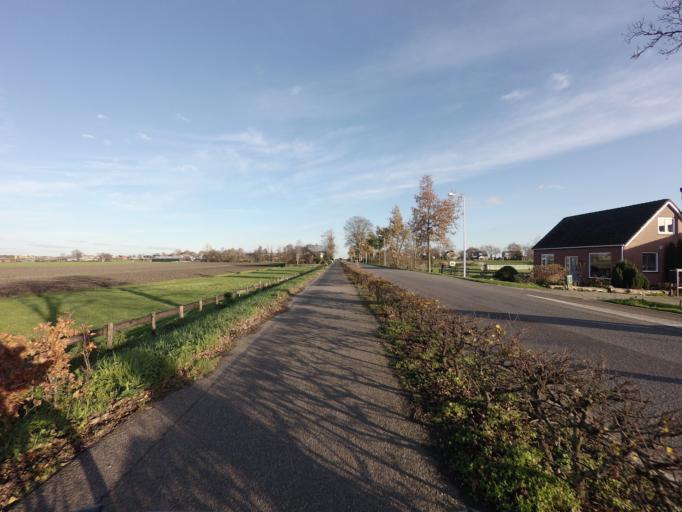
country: NL
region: South Holland
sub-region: Gemeente Nieuwkoop
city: Nieuwkoop
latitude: 52.1664
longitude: 4.7237
